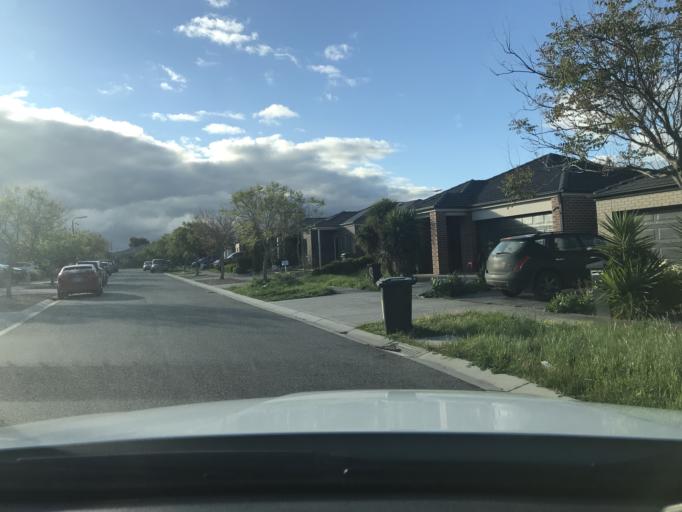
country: AU
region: Victoria
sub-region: Hume
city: Craigieburn
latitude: -37.5799
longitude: 144.9068
